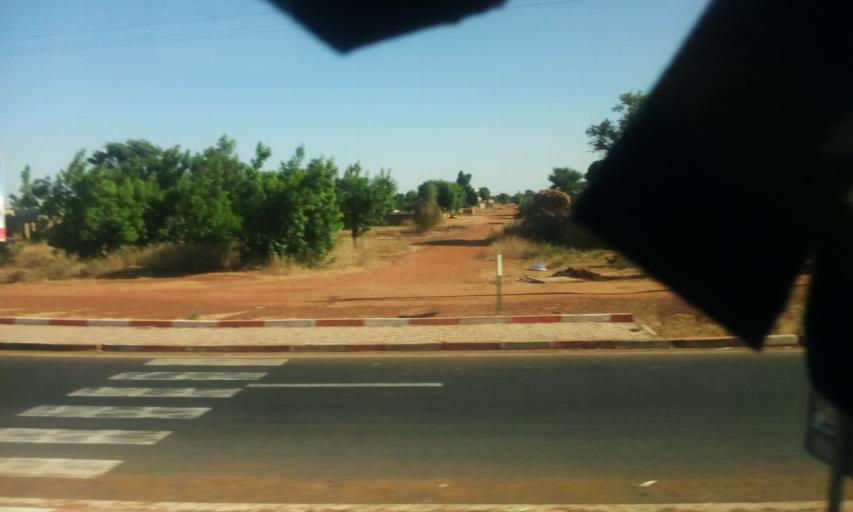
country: ML
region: Segou
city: Segou
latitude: 13.4144
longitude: -6.3233
